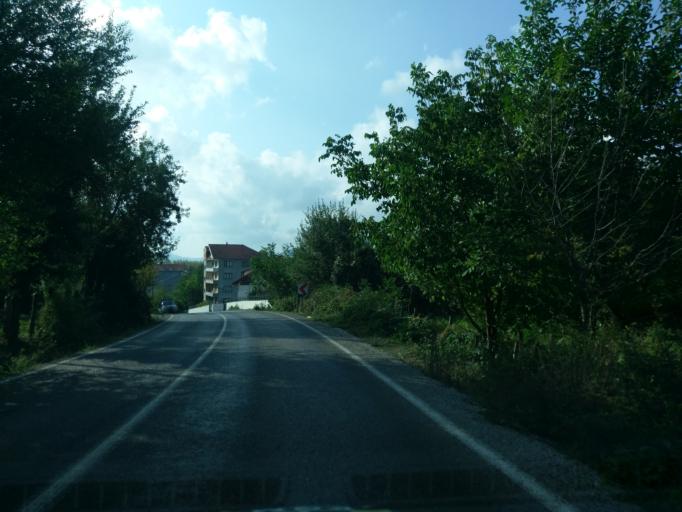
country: TR
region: Sinop
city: Helaldi
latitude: 41.8955
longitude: 34.4739
